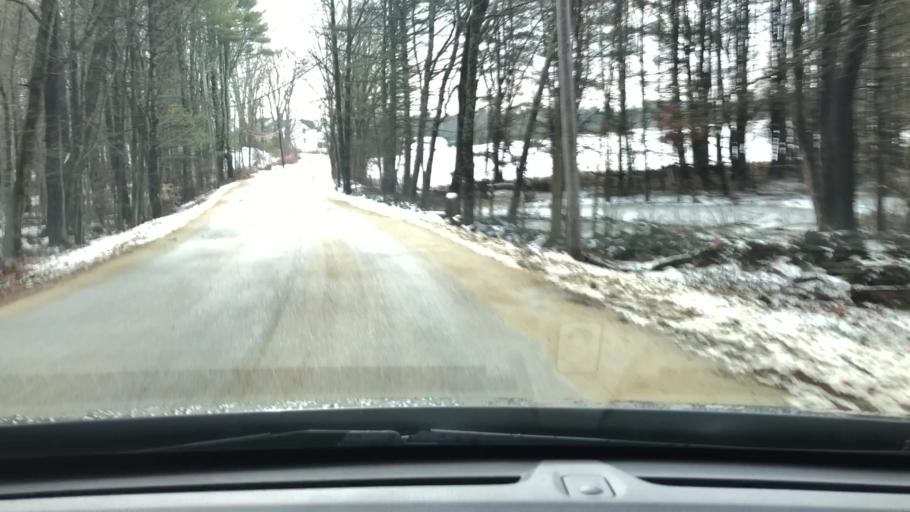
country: US
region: New Hampshire
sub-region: Strafford County
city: Madbury
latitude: 43.1876
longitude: -70.9779
